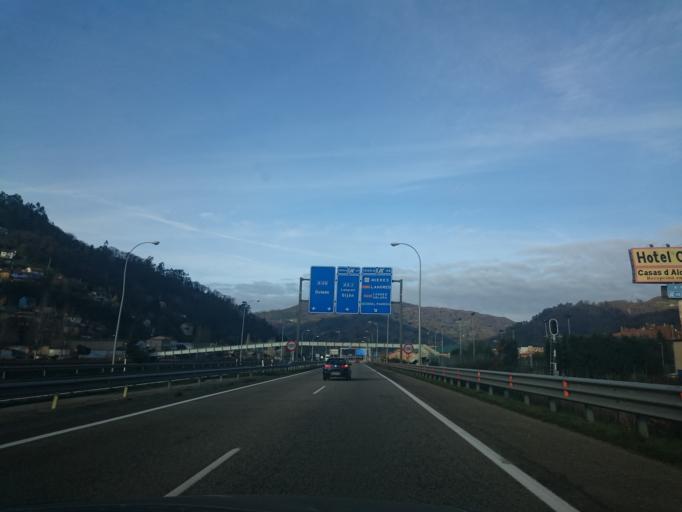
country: ES
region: Asturias
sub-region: Province of Asturias
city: Mieres
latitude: 43.2424
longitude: -5.7795
